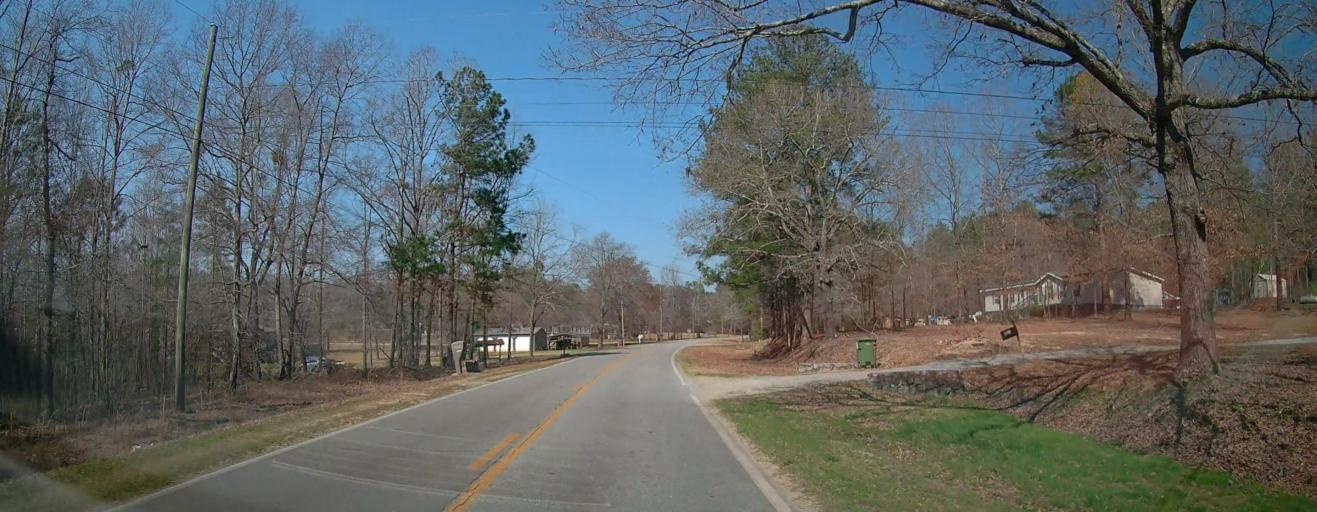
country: US
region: Georgia
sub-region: Bibb County
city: Macon
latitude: 32.8925
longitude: -83.5423
